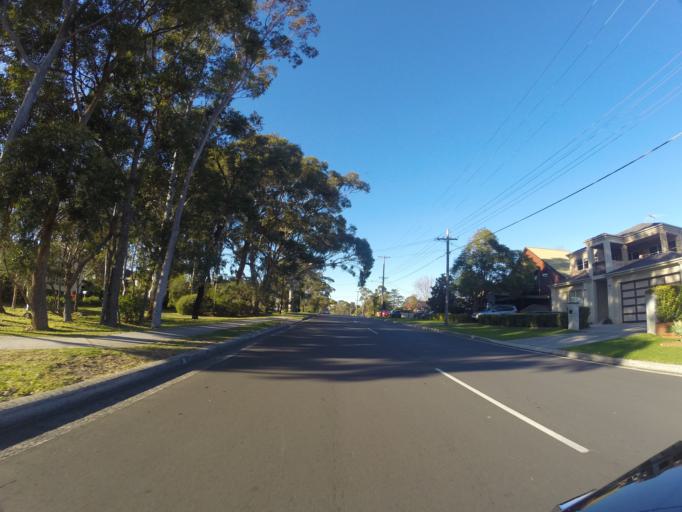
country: AU
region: New South Wales
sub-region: Sutherland Shire
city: Miranda
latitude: -34.0495
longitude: 151.1027
